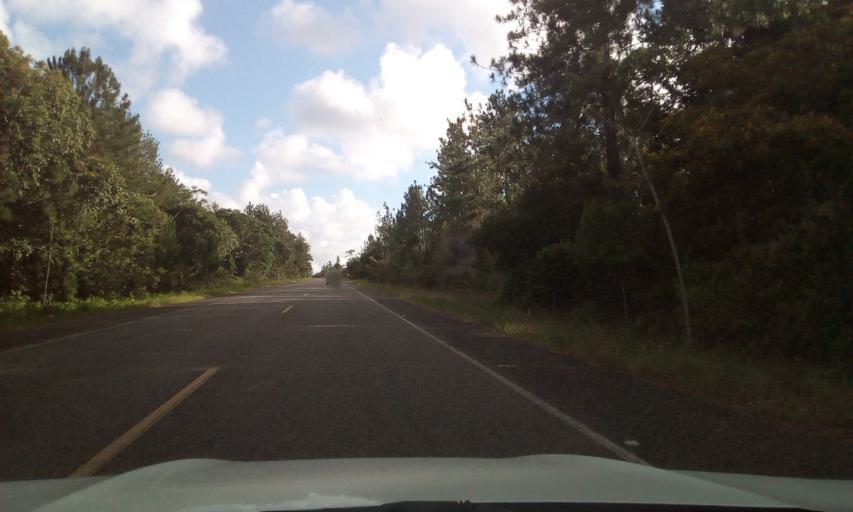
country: BR
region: Bahia
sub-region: Entre Rios
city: Entre Rios
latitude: -12.1459
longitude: -37.7953
